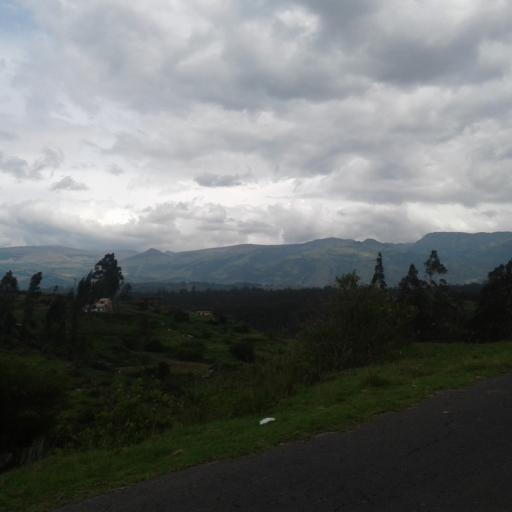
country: EC
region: Pichincha
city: Sangolqui
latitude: -0.2908
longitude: -78.3871
